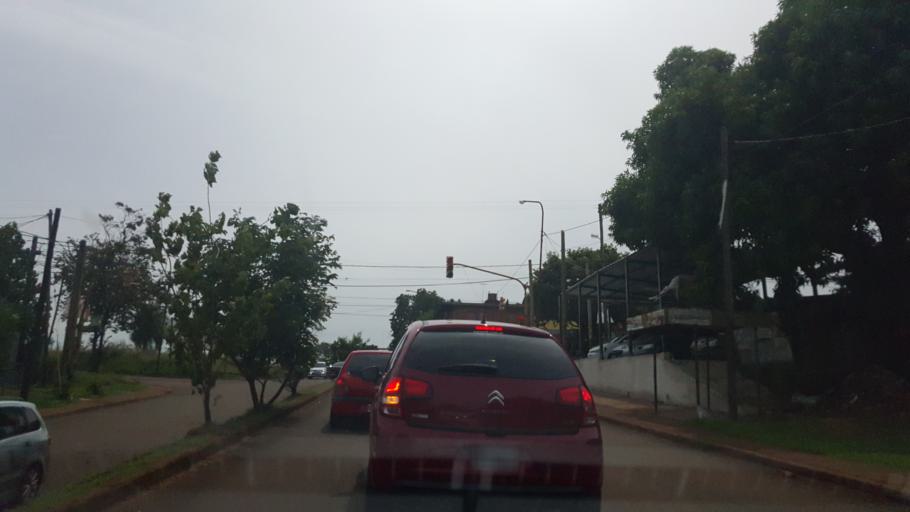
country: AR
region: Misiones
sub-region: Departamento de Capital
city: Posadas
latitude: -27.3835
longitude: -55.9416
